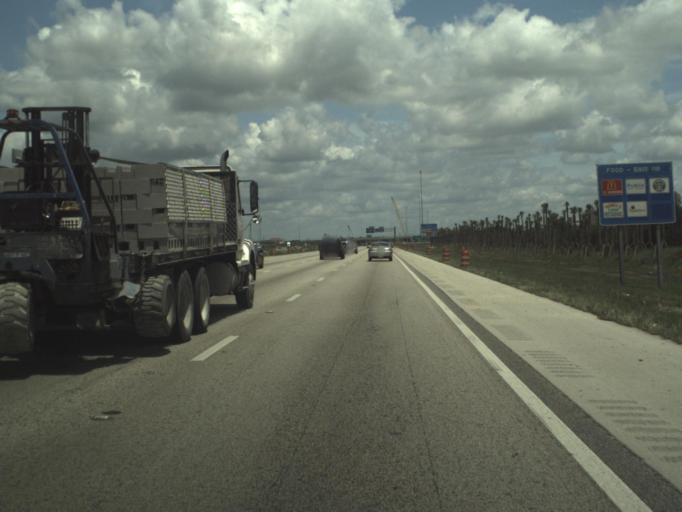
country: US
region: Florida
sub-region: Broward County
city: Sunshine Ranches
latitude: 26.0192
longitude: -80.3461
